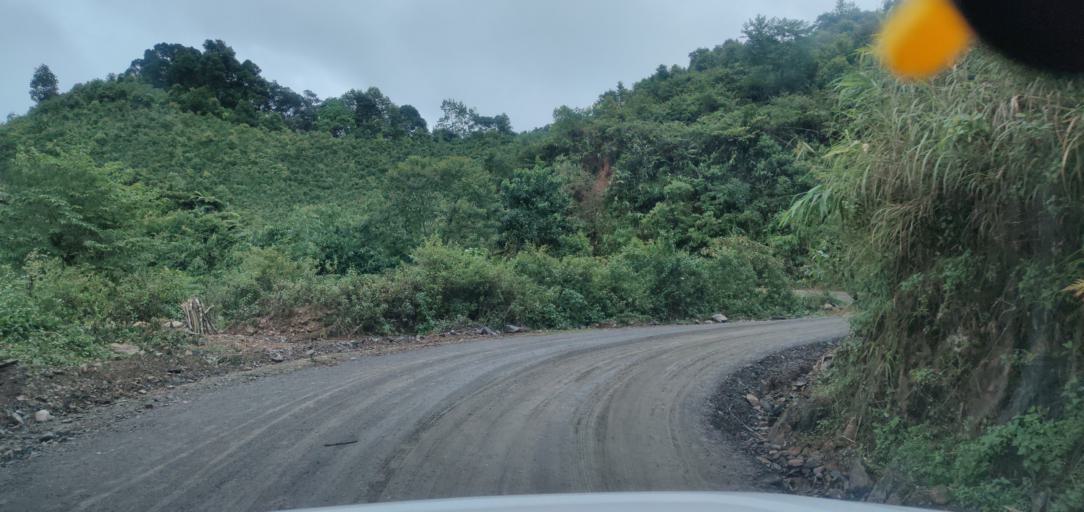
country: LA
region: Phongsali
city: Phongsali
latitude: 21.4289
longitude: 102.1640
